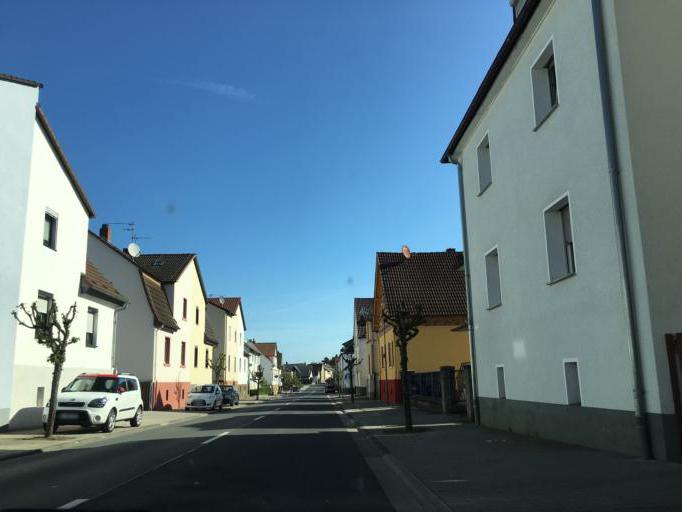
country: DE
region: Hesse
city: Obertshausen
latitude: 50.0930
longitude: 8.8539
